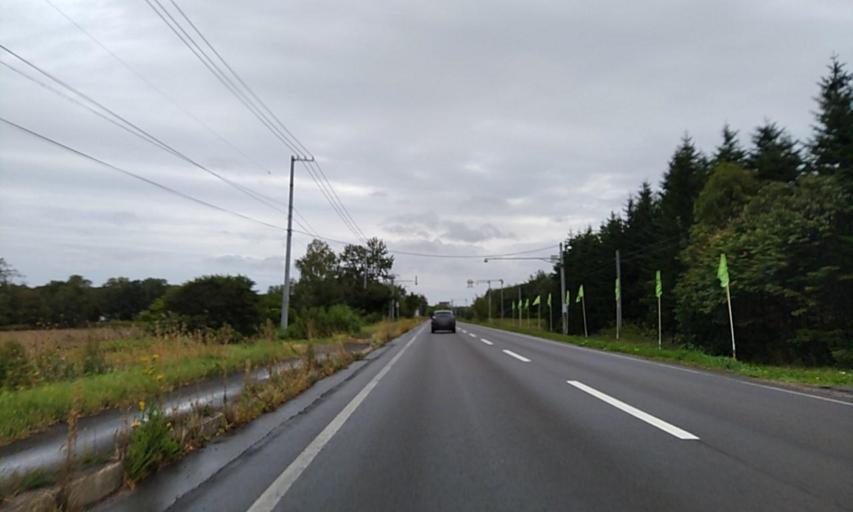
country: JP
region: Hokkaido
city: Kitami
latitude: 44.0852
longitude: 143.9496
